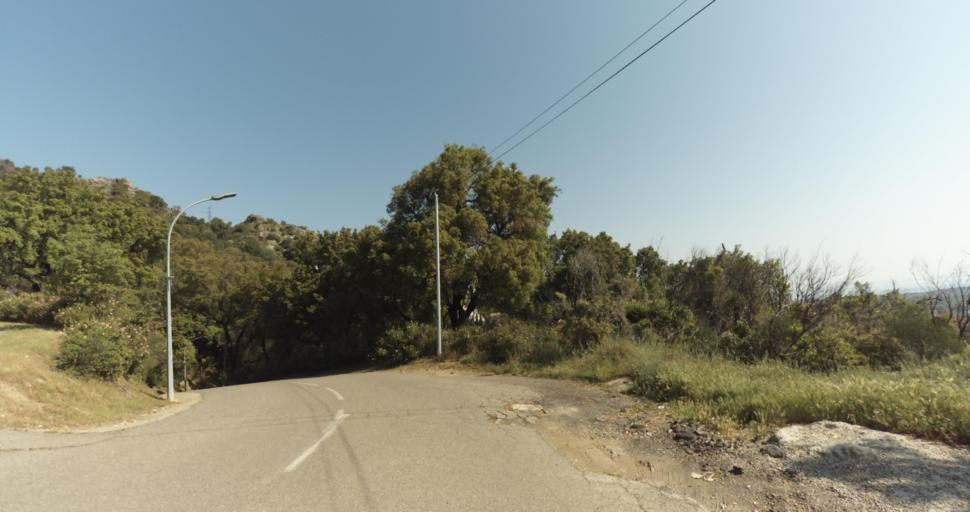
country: FR
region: Corsica
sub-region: Departement de la Haute-Corse
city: Biguglia
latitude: 42.6234
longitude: 9.4205
